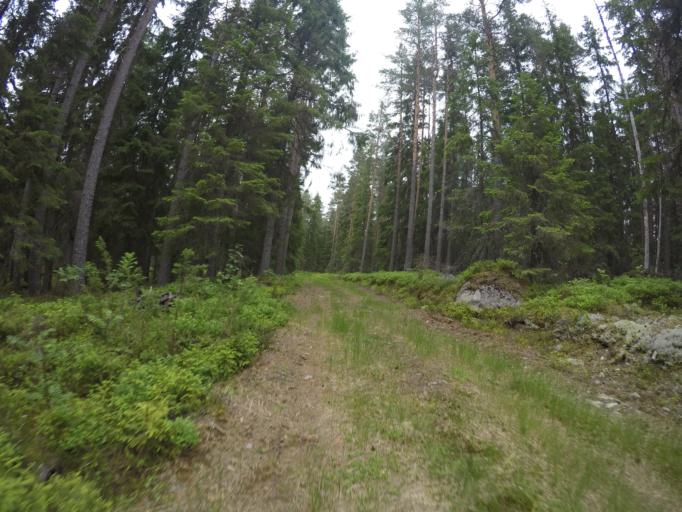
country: SE
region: Dalarna
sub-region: Ludvika Kommun
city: Abborrberget
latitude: 60.0668
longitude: 14.5312
